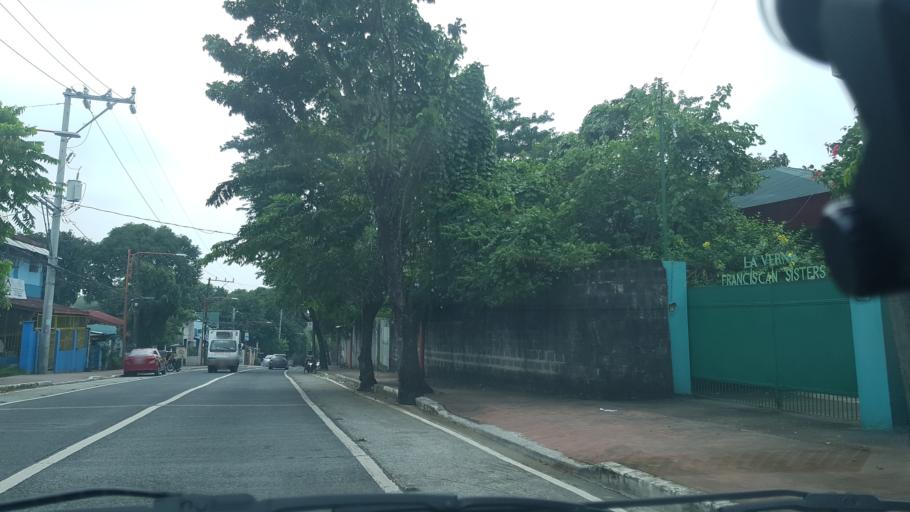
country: PH
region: Calabarzon
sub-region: Province of Rizal
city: Antipolo
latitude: 14.6537
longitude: 121.1230
